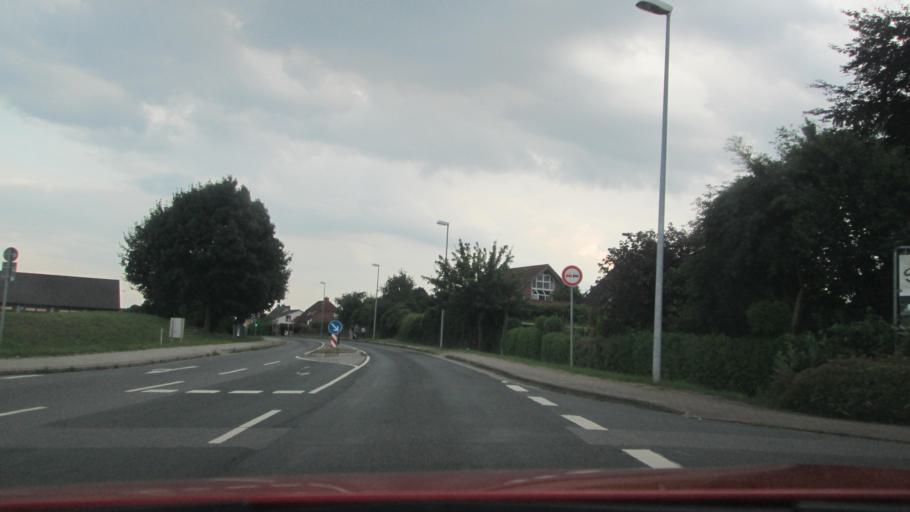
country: DE
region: Lower Saxony
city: Wolfsburg
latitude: 52.3630
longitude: 10.7490
